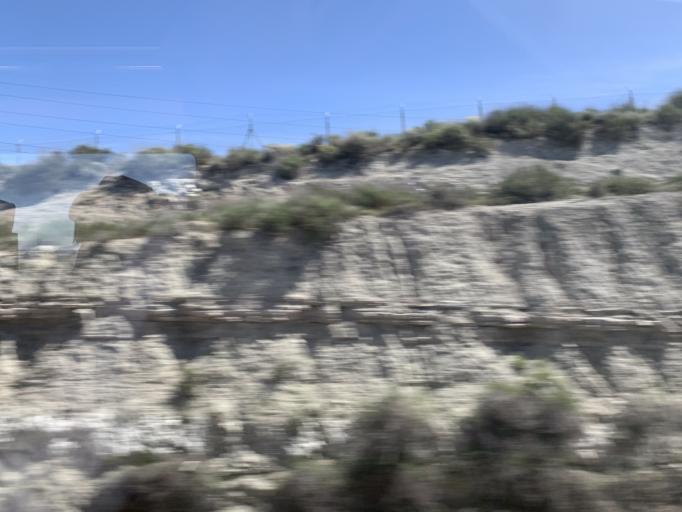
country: ES
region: Aragon
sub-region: Provincia de Huesca
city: Valfarta
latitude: 41.5271
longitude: -0.0967
